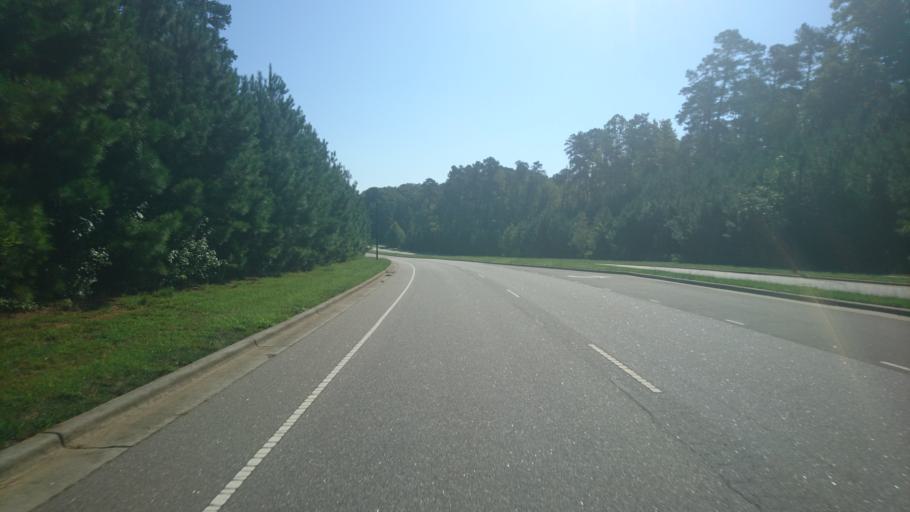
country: US
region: North Carolina
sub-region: Orange County
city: Hillsborough
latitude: 36.0374
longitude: -79.0876
